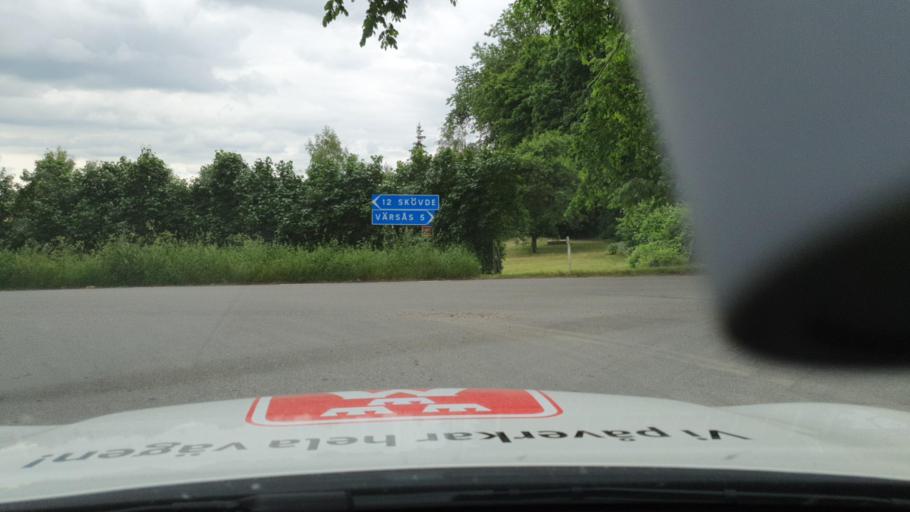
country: SE
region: Vaestra Goetaland
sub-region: Tidaholms Kommun
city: Olofstorp
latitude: 58.3355
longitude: 13.9838
